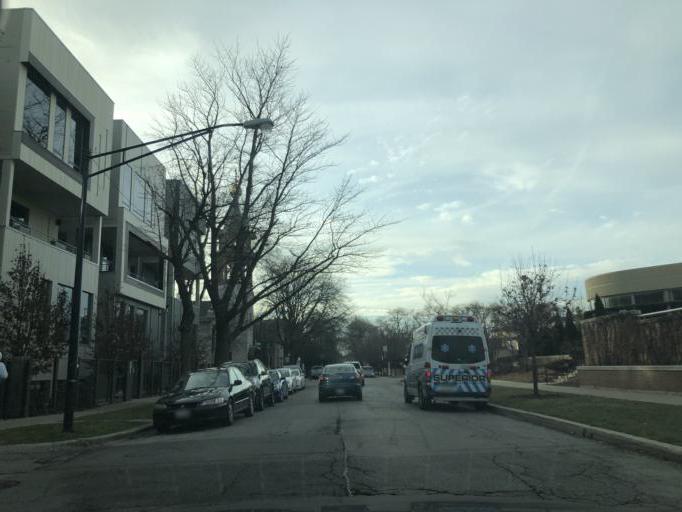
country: US
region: Illinois
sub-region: Cook County
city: Chicago
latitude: 41.9028
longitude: -87.6821
